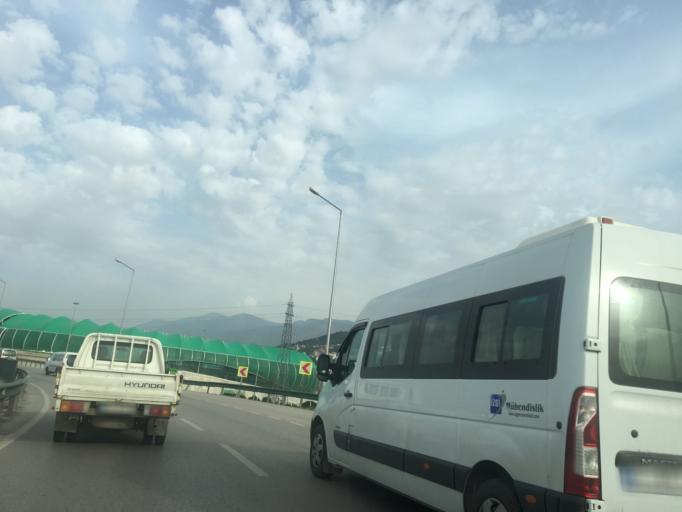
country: TR
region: Bursa
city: Yildirim
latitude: 40.2130
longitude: 29.0042
